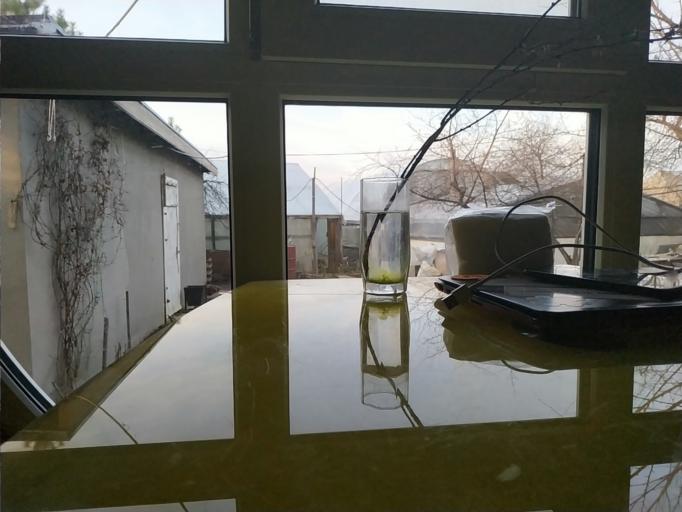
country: RU
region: Republic of Karelia
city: Suoyarvi
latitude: 62.3475
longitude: 32.0508
